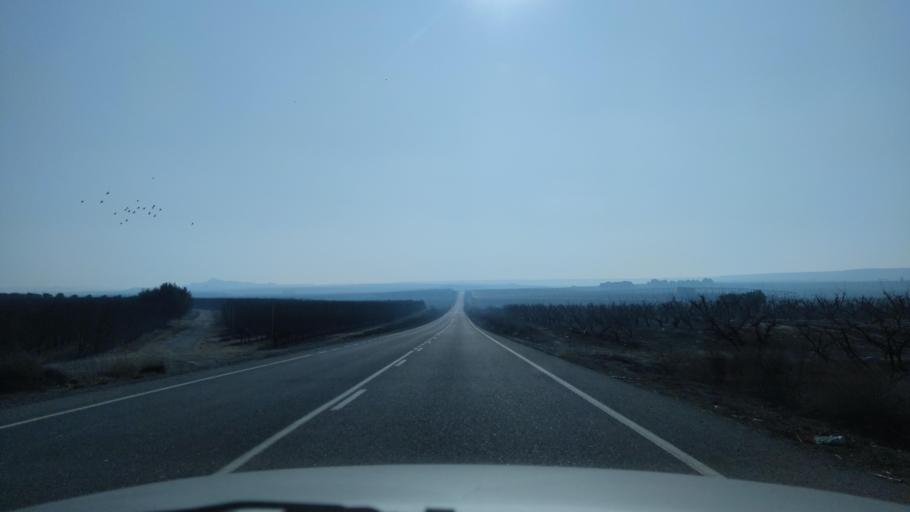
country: ES
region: Catalonia
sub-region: Provincia de Lleida
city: Sunyer
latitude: 41.5447
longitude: 0.5754
